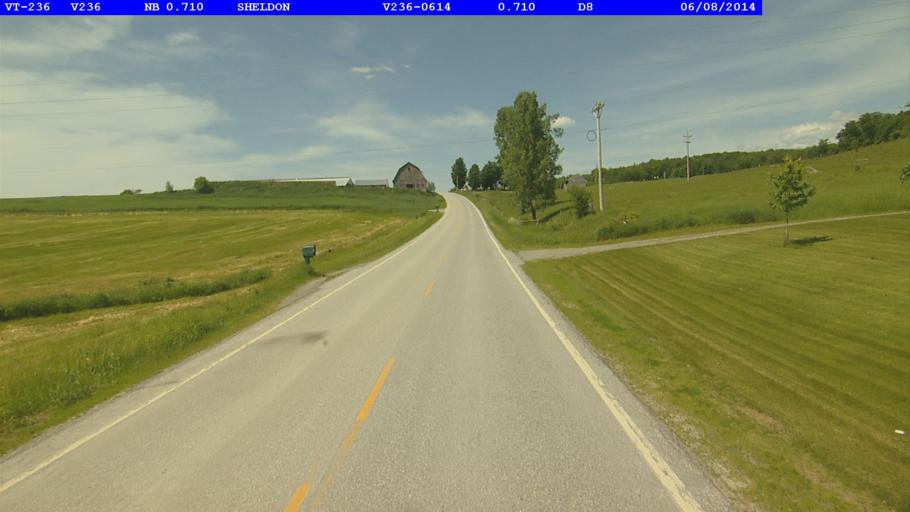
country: US
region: Vermont
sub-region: Franklin County
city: Enosburg Falls
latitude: 44.9211
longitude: -72.8652
